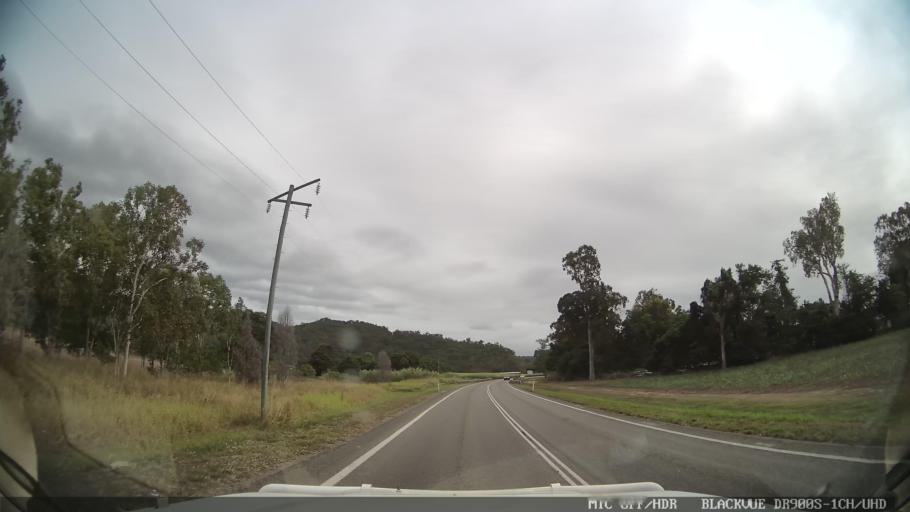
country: AU
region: Queensland
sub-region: Hinchinbrook
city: Ingham
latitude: -18.8626
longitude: 146.1706
